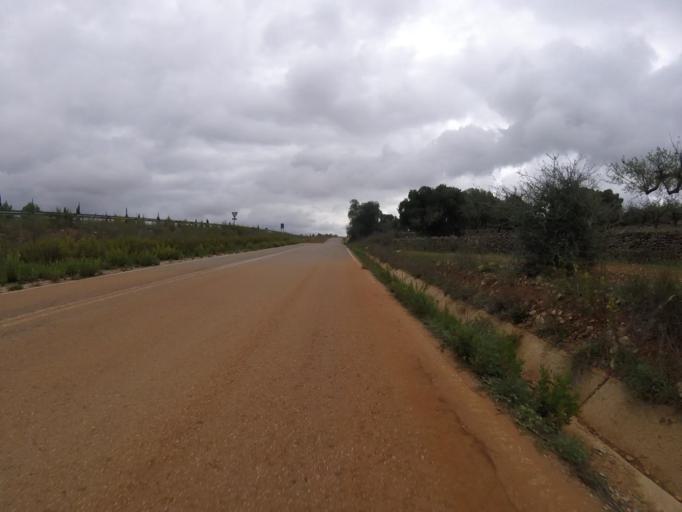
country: ES
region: Valencia
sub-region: Provincia de Castello
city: Cabanes
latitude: 40.1681
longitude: 0.0422
